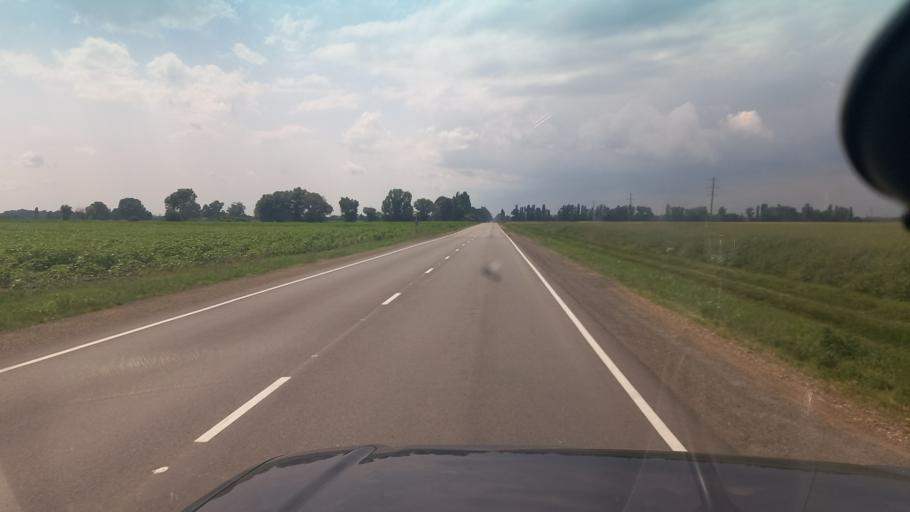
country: RU
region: Adygeya
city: Koshekhabl'
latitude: 44.9089
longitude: 40.4548
